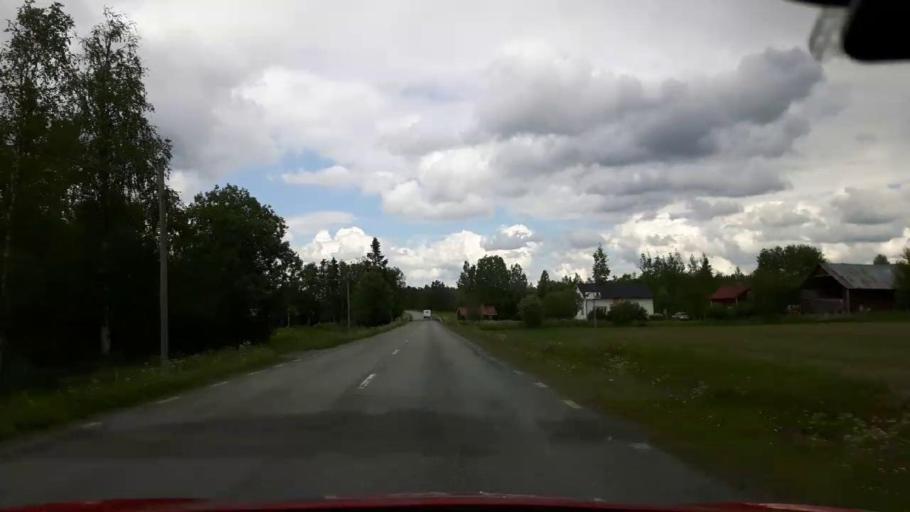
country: SE
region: Jaemtland
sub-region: Krokoms Kommun
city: Krokom
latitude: 63.5132
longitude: 14.2271
